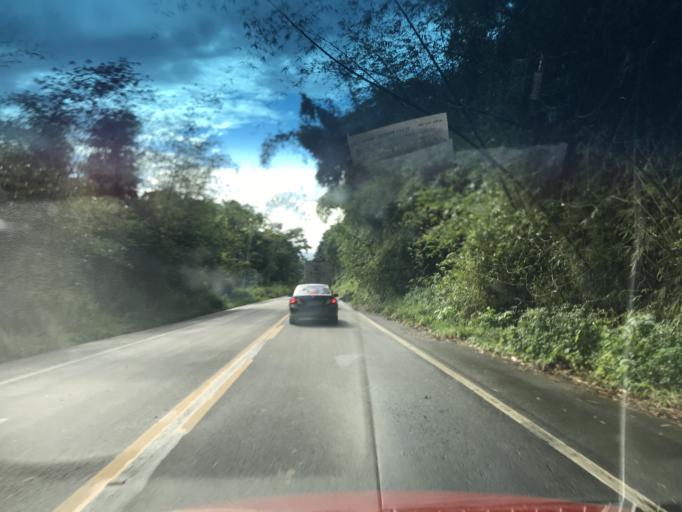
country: BR
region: Bahia
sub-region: Ibirapitanga
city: Ibirapitanga
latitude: -14.1800
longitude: -39.3198
